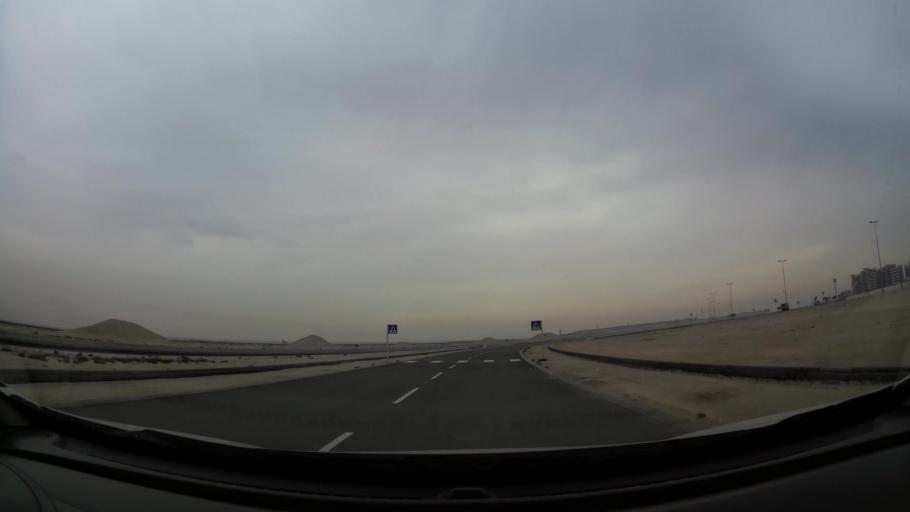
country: BH
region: Central Governorate
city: Dar Kulayb
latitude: 25.8638
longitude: 50.6047
